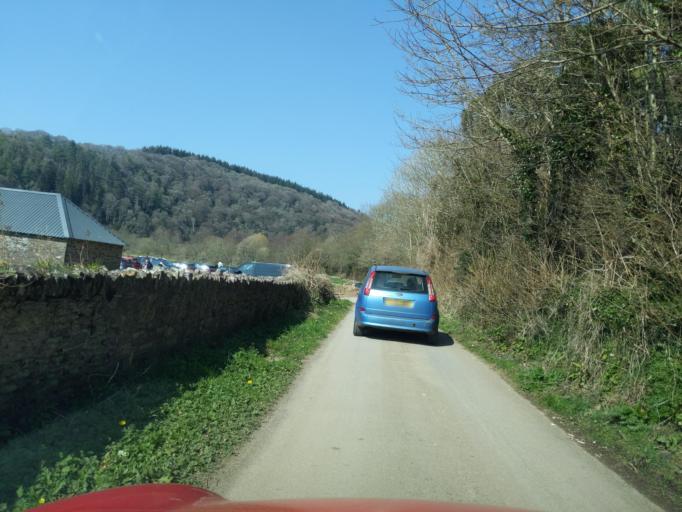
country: GB
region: England
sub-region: Devon
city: Bere Alston
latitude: 50.4582
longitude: -4.1543
